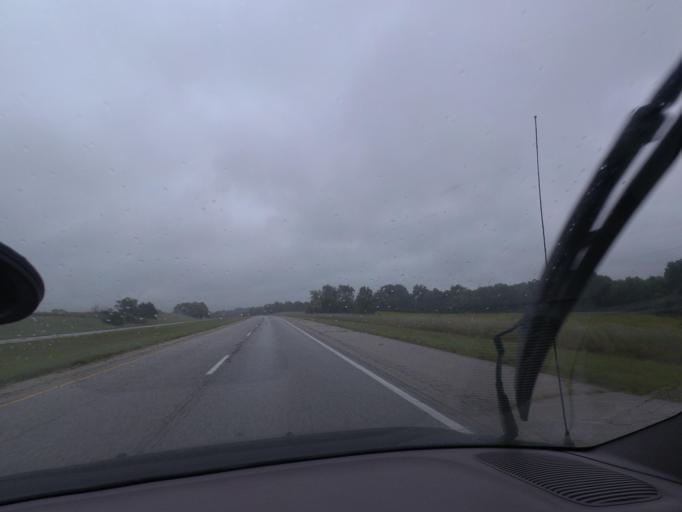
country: US
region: Illinois
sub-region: Pike County
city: Pittsfield
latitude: 39.6765
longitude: -90.8638
